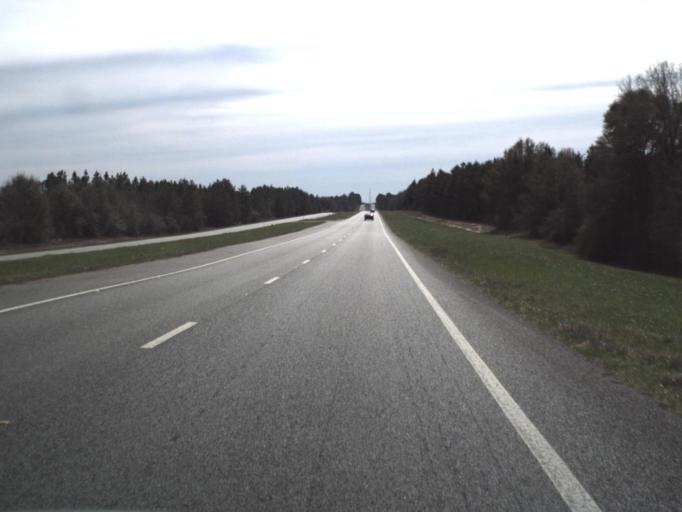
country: US
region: Florida
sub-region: Bay County
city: Youngstown
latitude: 30.5743
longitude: -85.3872
